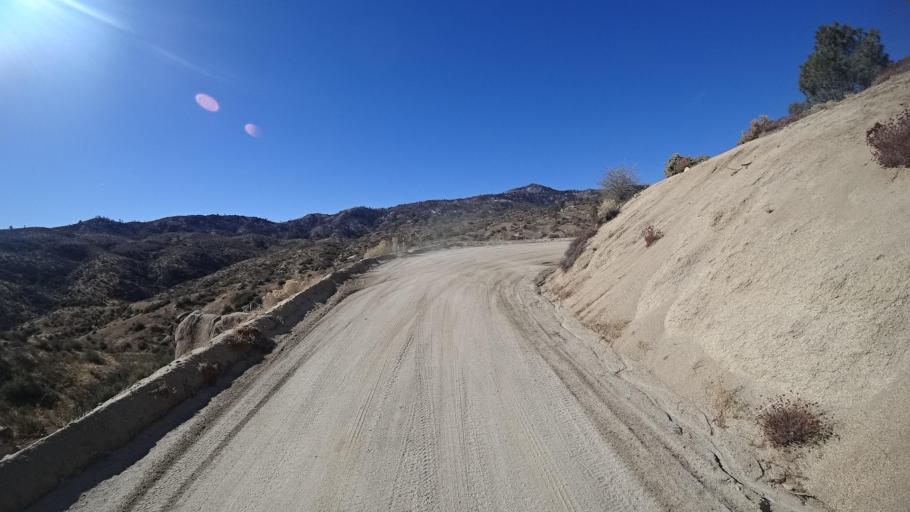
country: US
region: California
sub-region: Kern County
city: Wofford Heights
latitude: 35.7053
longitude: -118.4950
